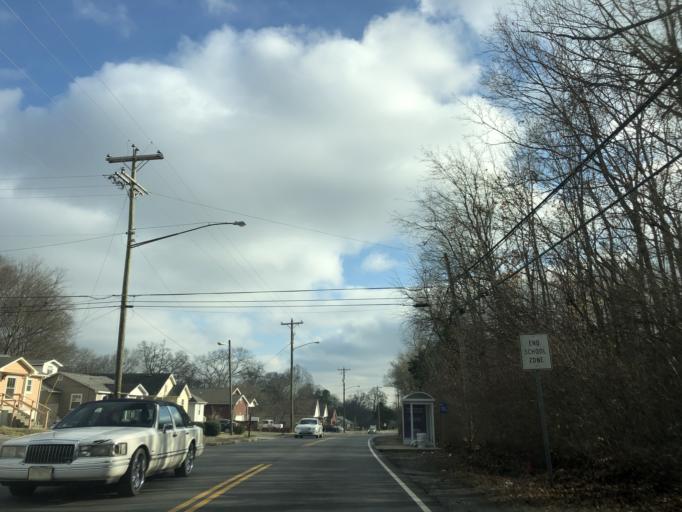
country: US
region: Tennessee
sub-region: Davidson County
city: Nashville
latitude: 36.2062
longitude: -86.7909
